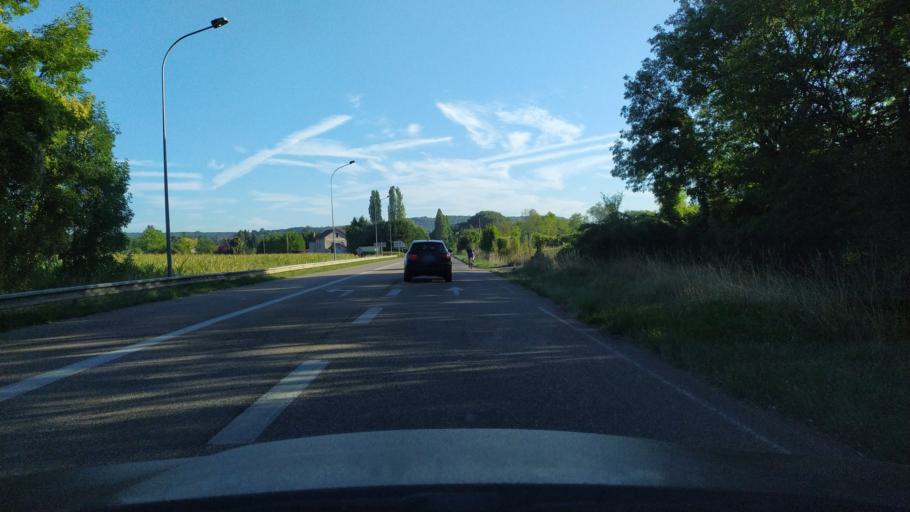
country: FR
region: Lorraine
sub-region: Departement de la Moselle
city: Rozerieulles
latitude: 49.0886
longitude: 6.0916
